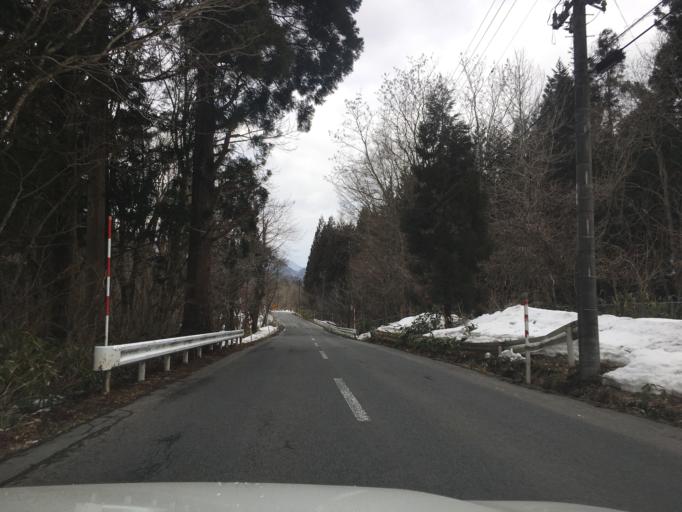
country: JP
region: Akita
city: Odate
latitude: 40.4314
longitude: 140.6443
